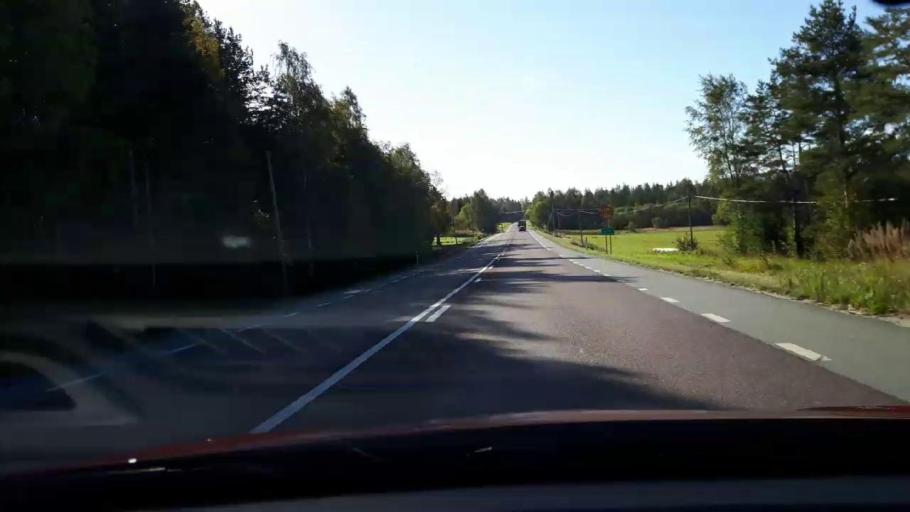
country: SE
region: Jaemtland
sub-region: Braecke Kommun
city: Braecke
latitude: 62.7891
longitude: 15.3795
